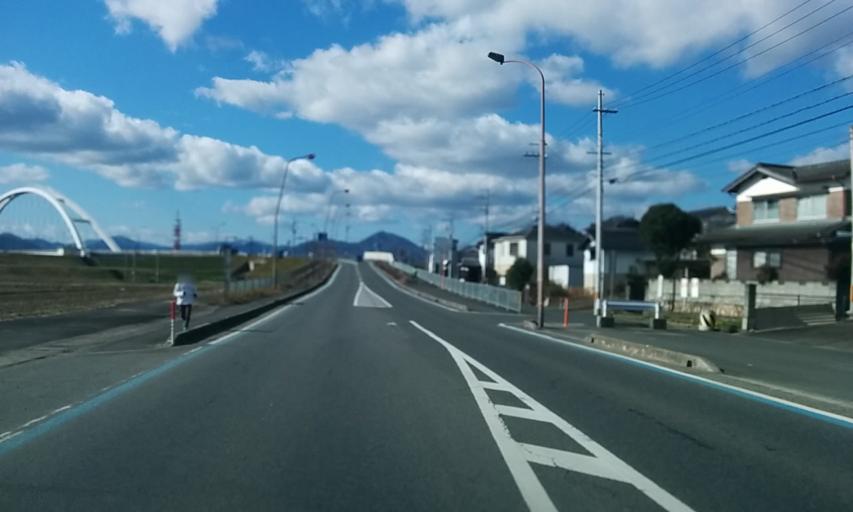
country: JP
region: Kyoto
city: Fukuchiyama
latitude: 35.3048
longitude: 135.1347
